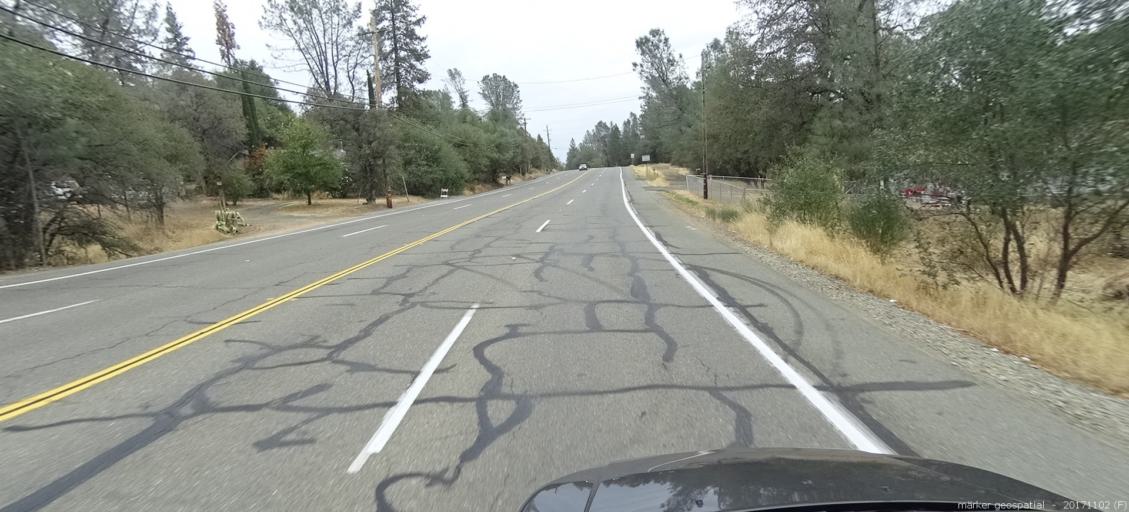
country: US
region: California
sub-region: Shasta County
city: Redding
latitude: 40.6366
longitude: -122.4040
